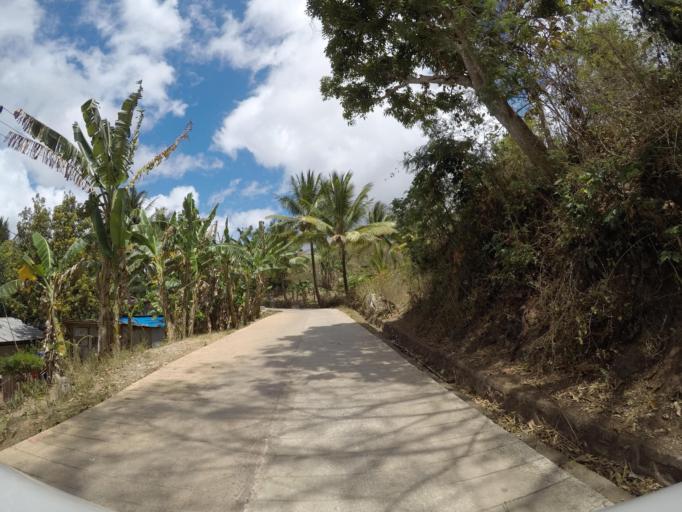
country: TL
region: Lautem
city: Lospalos
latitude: -8.5479
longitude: 126.8311
